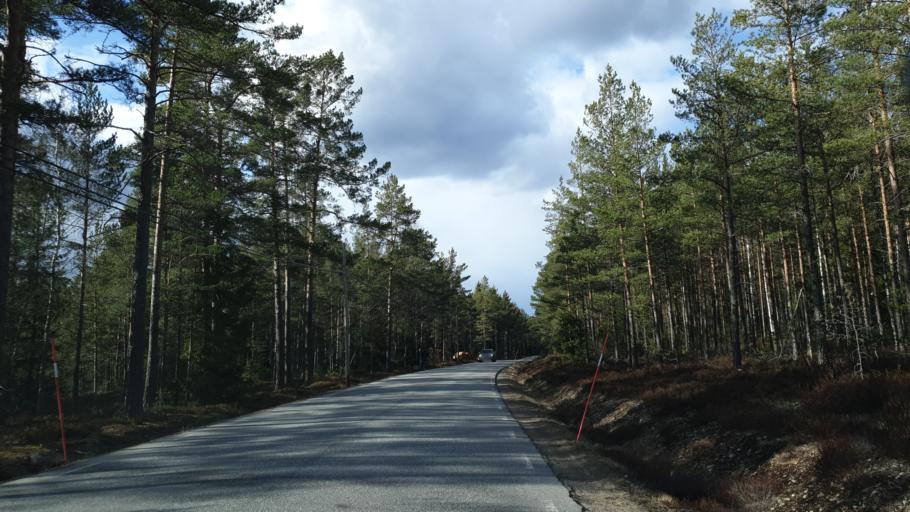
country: SE
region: Stockholm
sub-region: Varmdo Kommun
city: Mortnas
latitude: 59.2534
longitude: 18.4369
